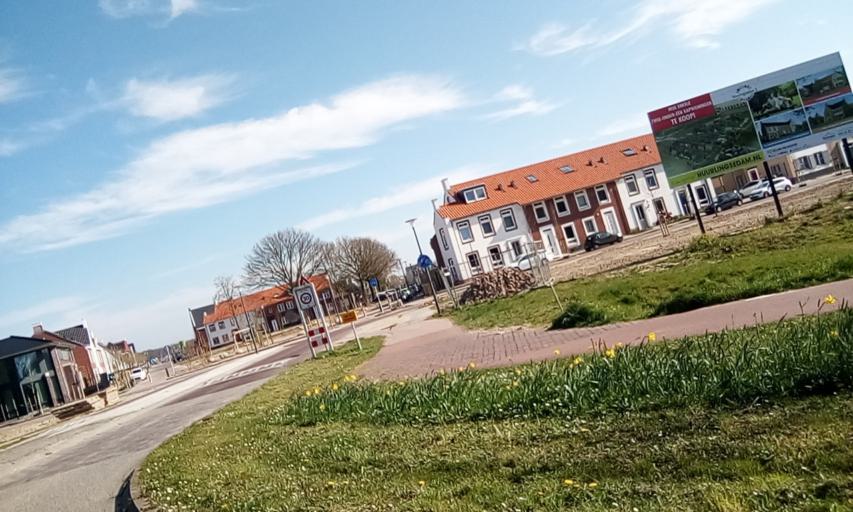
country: NL
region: Gelderland
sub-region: Gemeente Wijchen
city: Wijchen
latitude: 51.7999
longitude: 5.7378
